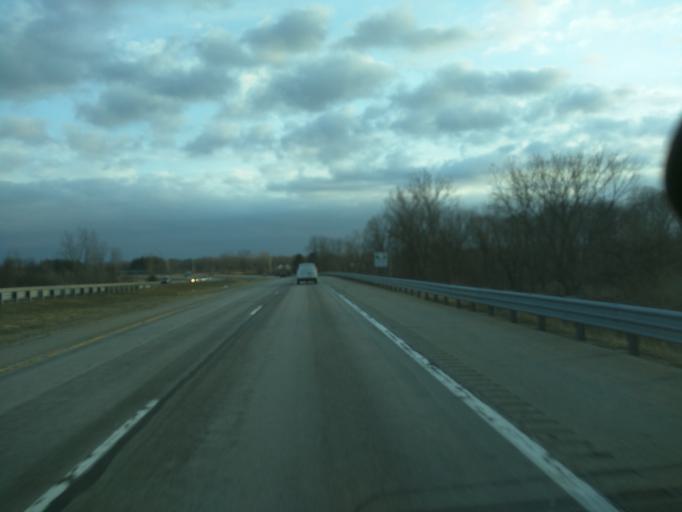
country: US
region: Michigan
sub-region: Ingham County
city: Holt
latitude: 42.6191
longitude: -84.4763
